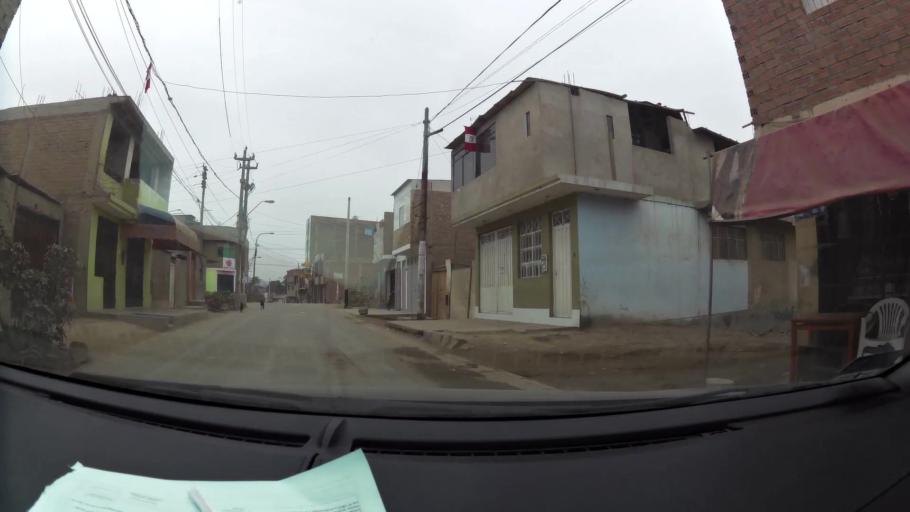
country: PE
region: Lima
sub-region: Lima
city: Urb. Santo Domingo
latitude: -11.8841
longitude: -77.0669
